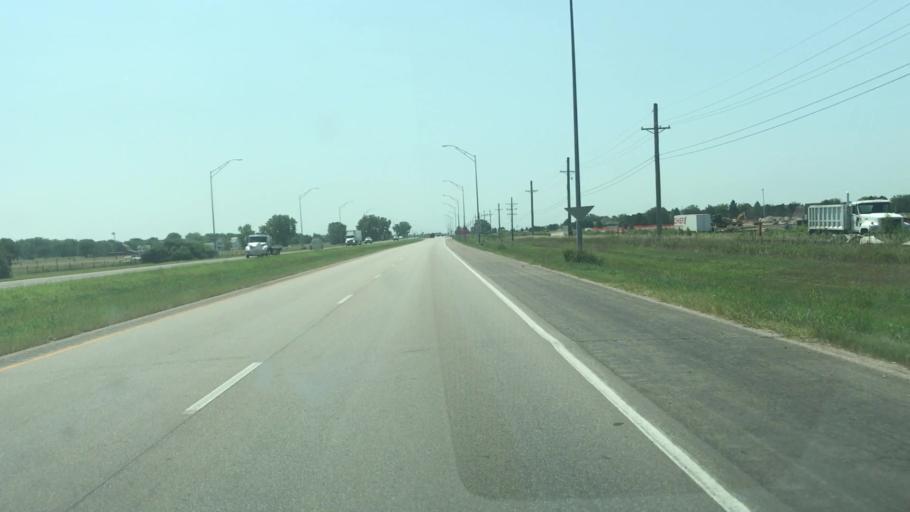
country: US
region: Nebraska
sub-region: Hall County
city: Grand Island
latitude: 40.8847
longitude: -98.3784
